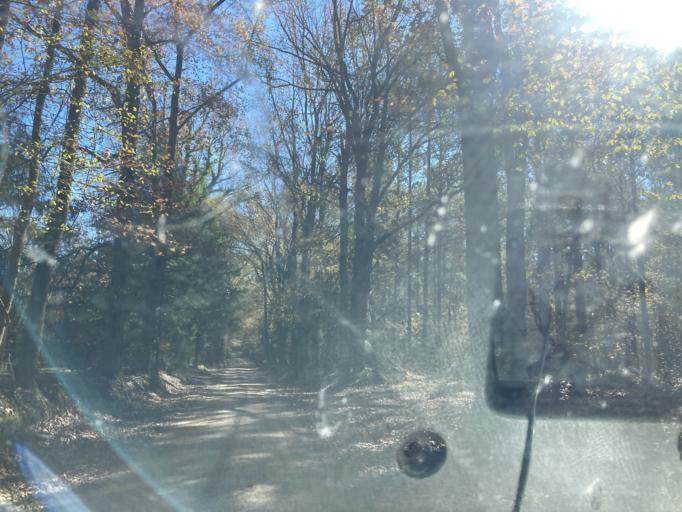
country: US
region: Mississippi
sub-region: Hinds County
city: Lynchburg
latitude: 32.5520
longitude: -90.4977
